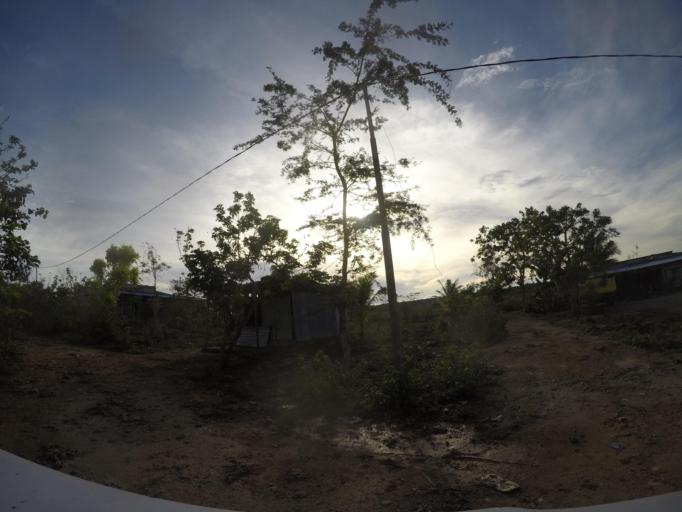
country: TL
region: Baucau
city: Baucau
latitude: -8.4868
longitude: 126.4506
